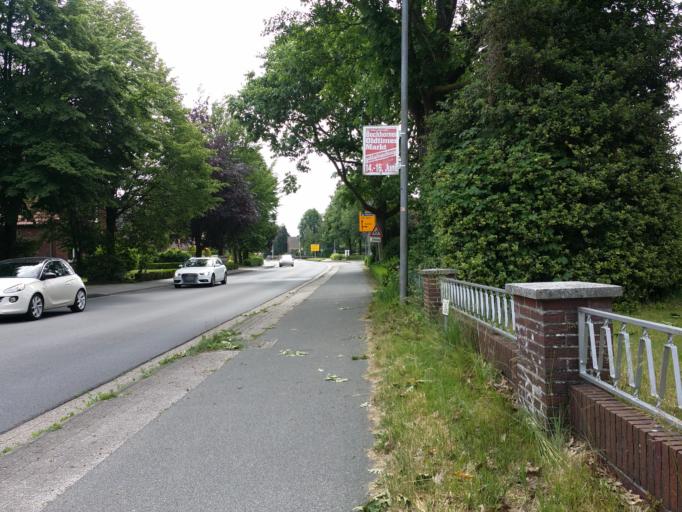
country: DE
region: Lower Saxony
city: Friedeburg
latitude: 53.4336
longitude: 7.8571
